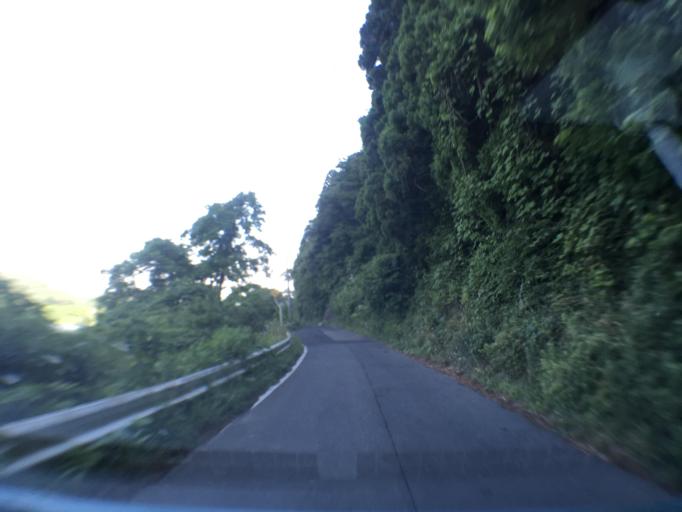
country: JP
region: Miyagi
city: Wakuya
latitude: 38.6318
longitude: 141.2869
